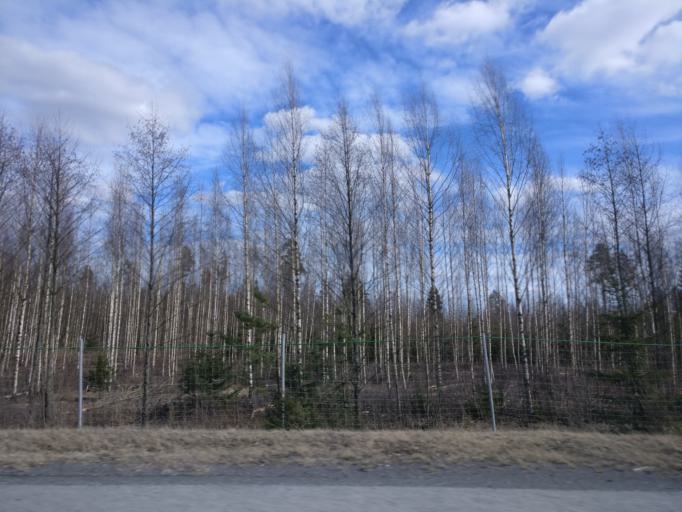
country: FI
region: Pirkanmaa
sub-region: Tampere
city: Lempaeaelae
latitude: 61.3053
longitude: 23.8240
